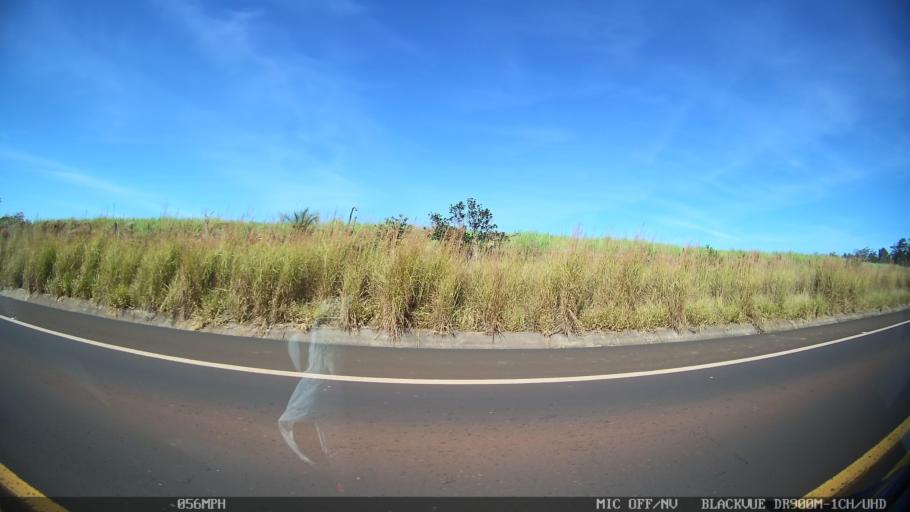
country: BR
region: Sao Paulo
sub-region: Franca
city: Franca
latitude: -20.5610
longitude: -47.5069
